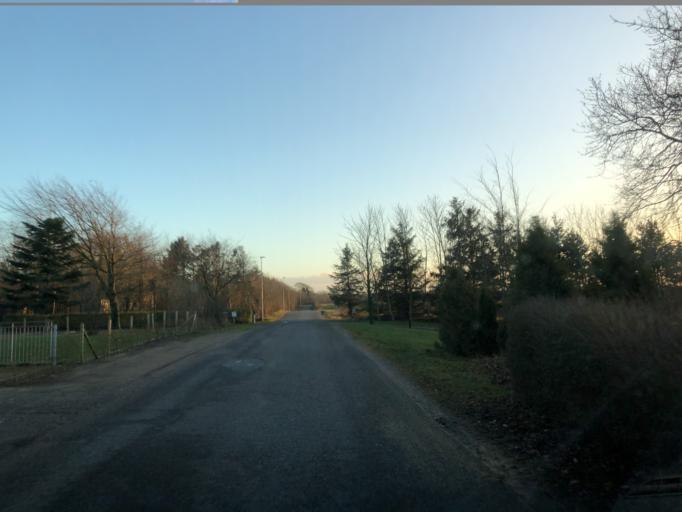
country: DK
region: Central Jutland
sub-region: Skive Kommune
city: Skive
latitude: 56.5396
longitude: 8.9313
